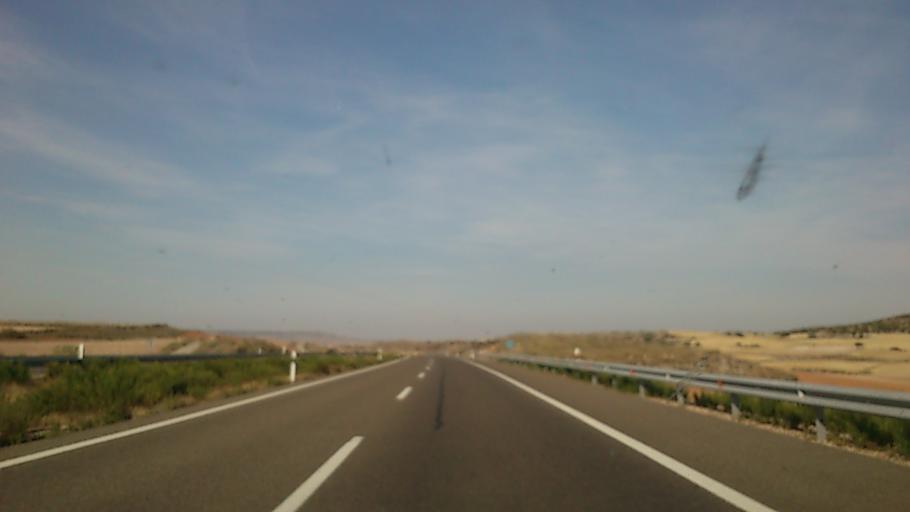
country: ES
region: Aragon
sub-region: Provincia de Zaragoza
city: Longares
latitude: 41.4216
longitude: -1.1534
